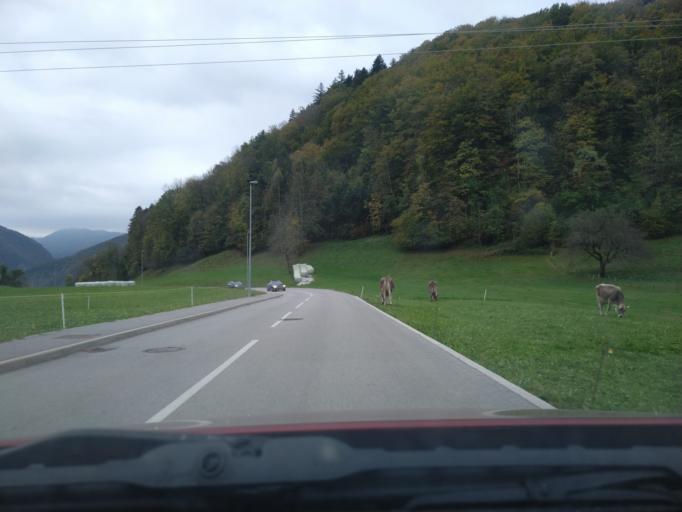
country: SI
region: Tolmin
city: Tolmin
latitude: 46.1933
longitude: 13.7279
